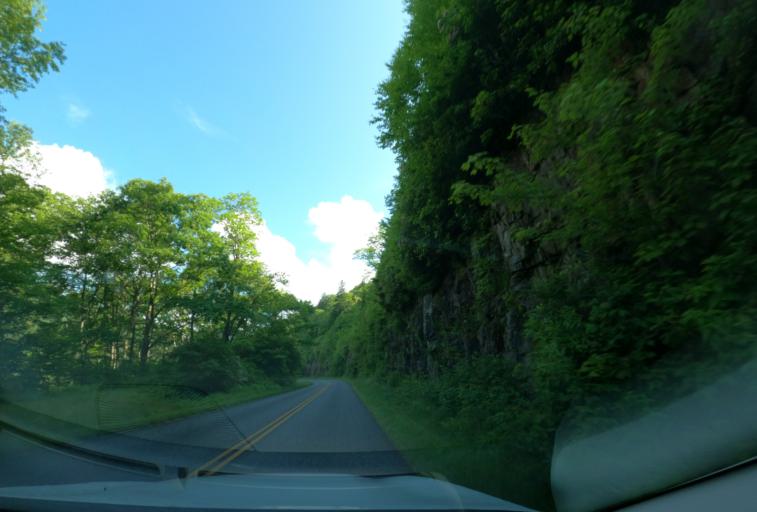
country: US
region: North Carolina
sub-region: Haywood County
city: Hazelwood
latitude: 35.3105
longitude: -82.9517
